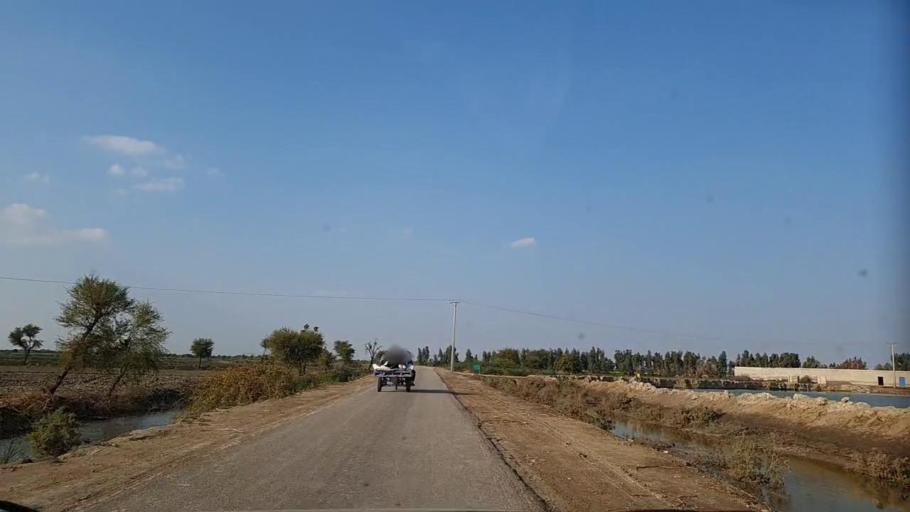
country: PK
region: Sindh
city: Pithoro
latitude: 25.7126
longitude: 69.2205
